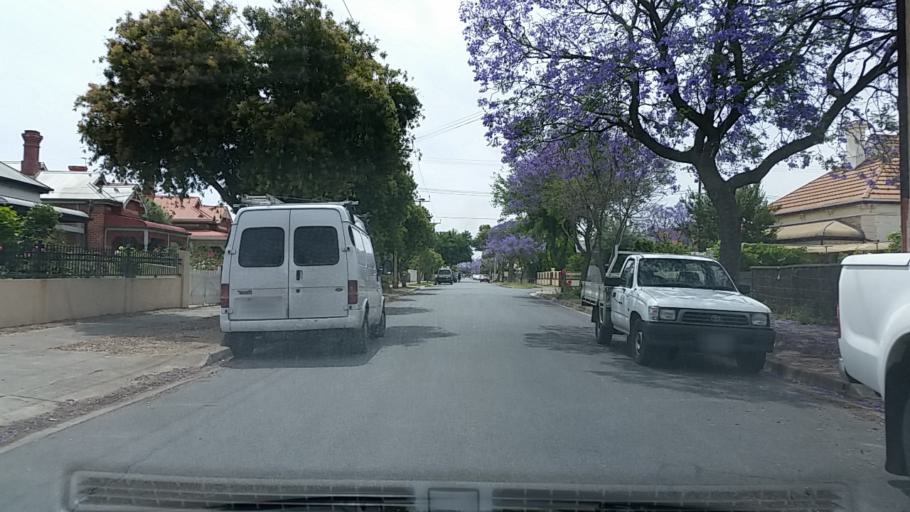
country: AU
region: South Australia
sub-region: Charles Sturt
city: Allenby Gardens
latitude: -34.8942
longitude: 138.5638
